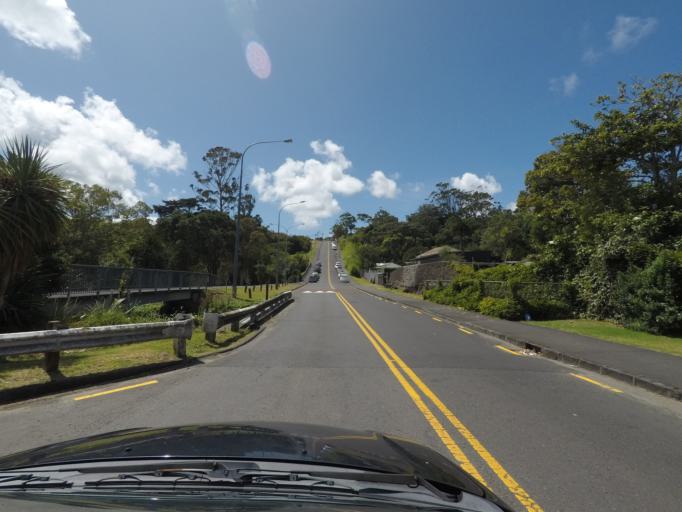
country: NZ
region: Auckland
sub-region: Auckland
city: Auckland
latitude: -36.8613
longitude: 174.7193
